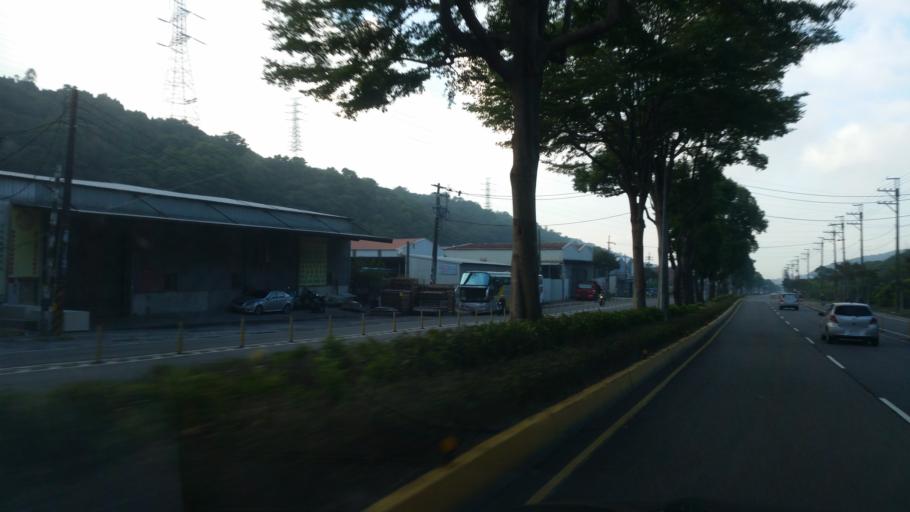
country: TW
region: Taiwan
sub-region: Taoyuan
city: Taoyuan
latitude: 25.0290
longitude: 121.3548
